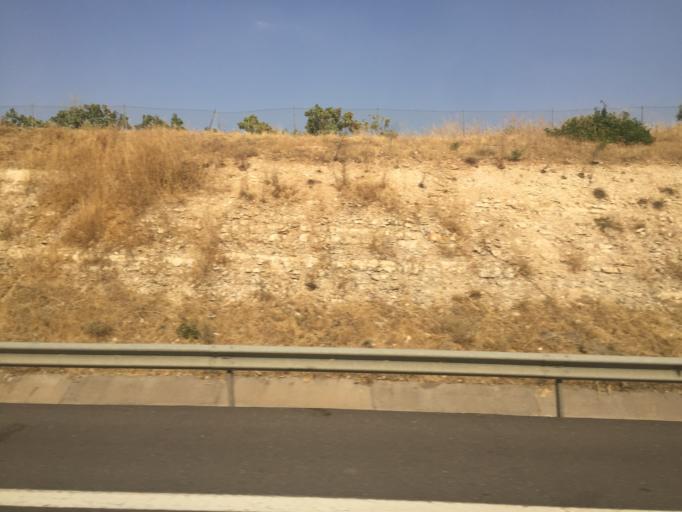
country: TR
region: Sanliurfa
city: Akziyaret
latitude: 37.2704
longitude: 38.8014
